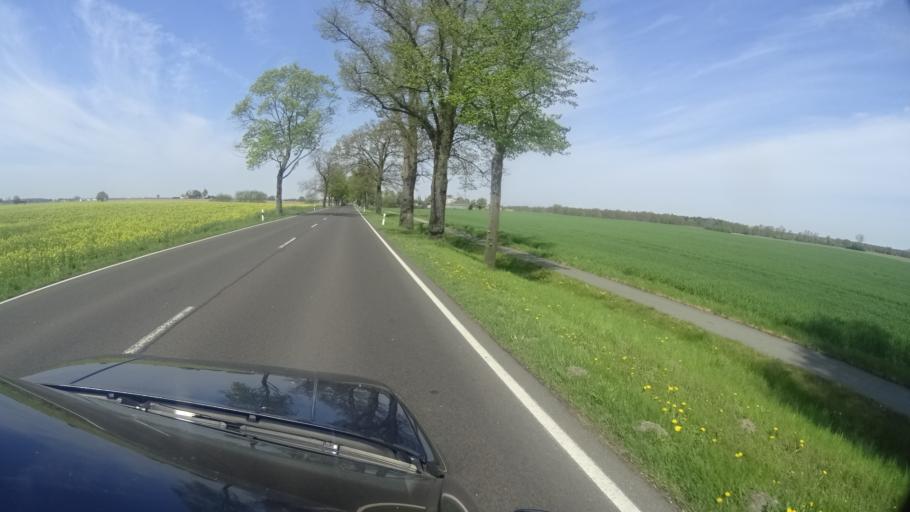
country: DE
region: Brandenburg
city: Retzow
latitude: 52.6351
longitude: 12.7016
